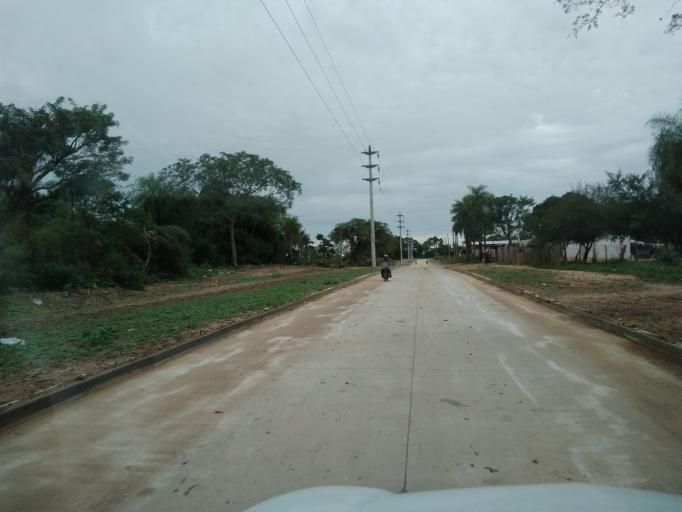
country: AR
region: Corrientes
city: Corrientes
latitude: -27.5145
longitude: -58.8215
